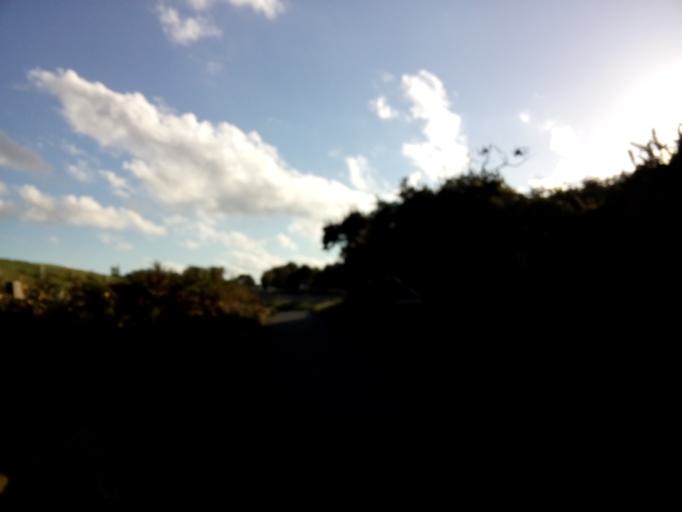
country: GB
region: England
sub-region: Suffolk
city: Kesgrave
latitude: 52.0548
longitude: 1.2780
